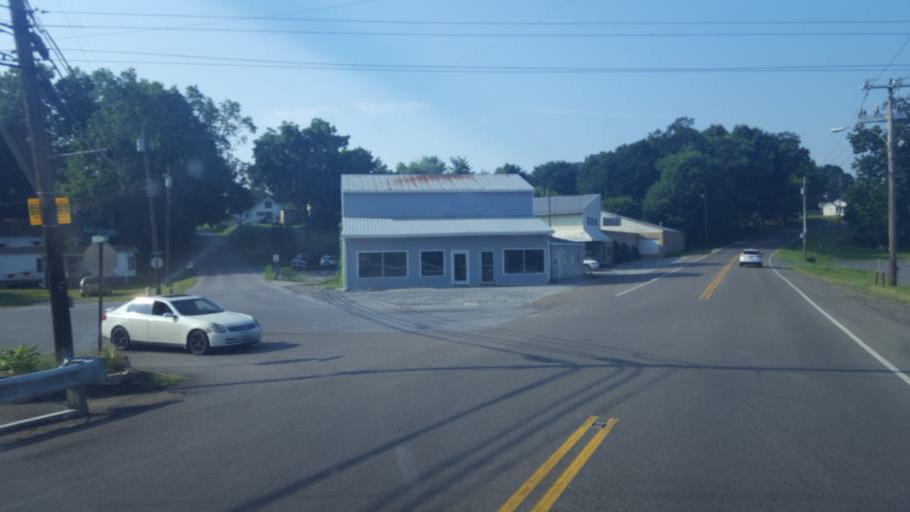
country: US
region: Tennessee
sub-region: Sullivan County
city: Bluff City
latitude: 36.4764
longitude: -82.2636
